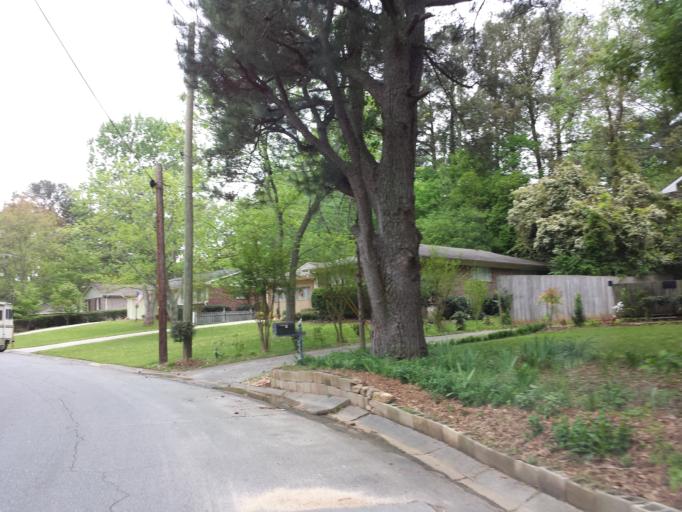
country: US
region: Georgia
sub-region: Cobb County
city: Marietta
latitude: 33.9466
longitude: -84.5721
